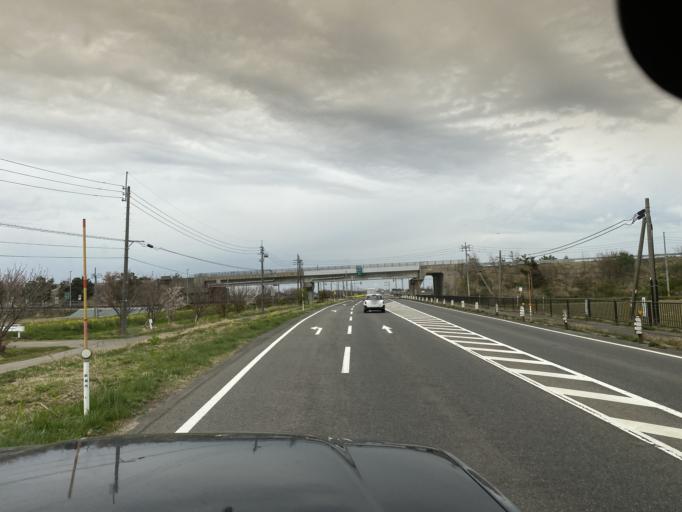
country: JP
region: Niigata
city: Niitsu-honcho
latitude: 37.8194
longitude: 139.0992
